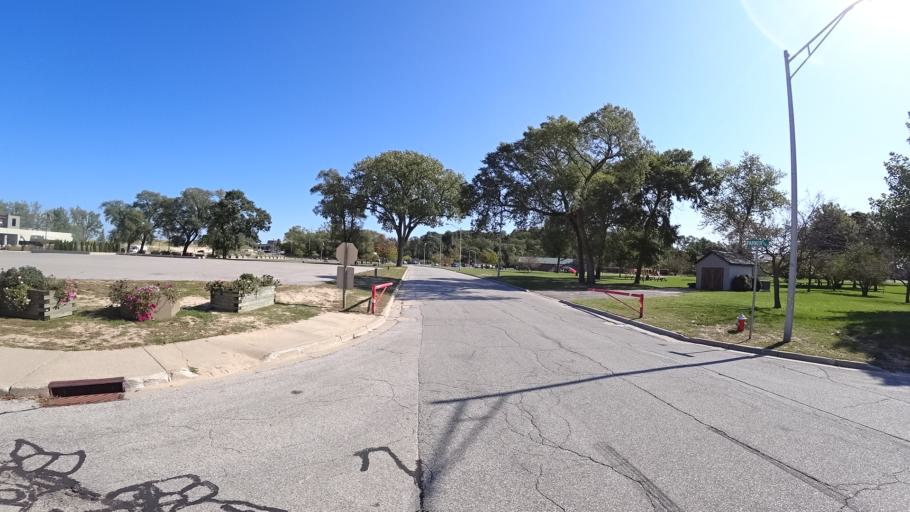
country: US
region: Indiana
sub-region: LaPorte County
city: Michigan City
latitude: 41.7259
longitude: -86.9034
